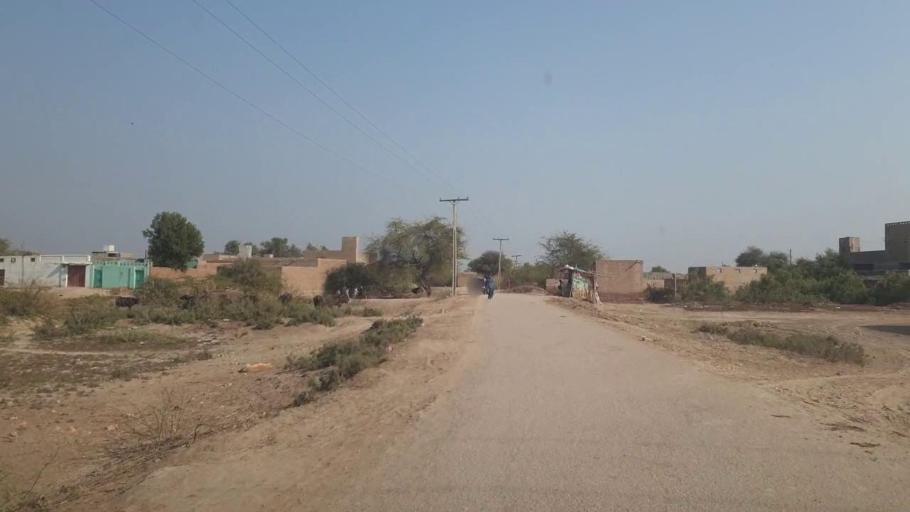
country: PK
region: Sindh
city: Tando Allahyar
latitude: 25.4390
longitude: 68.7110
